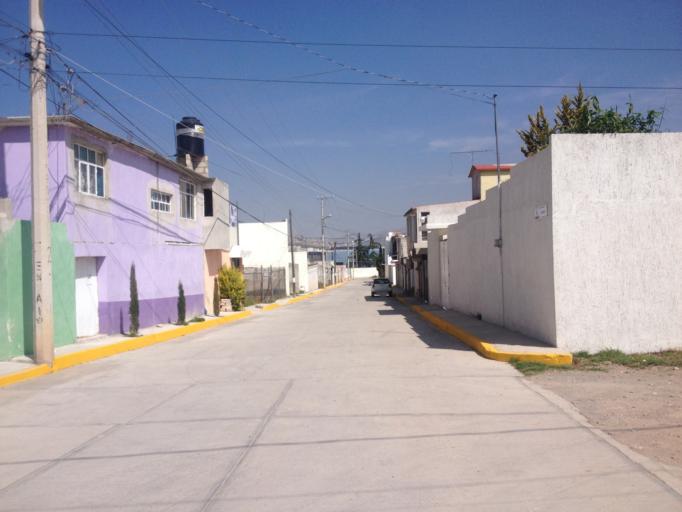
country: MX
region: Hidalgo
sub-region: Mineral de la Reforma
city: Carboneras
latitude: 20.0930
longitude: -98.7049
